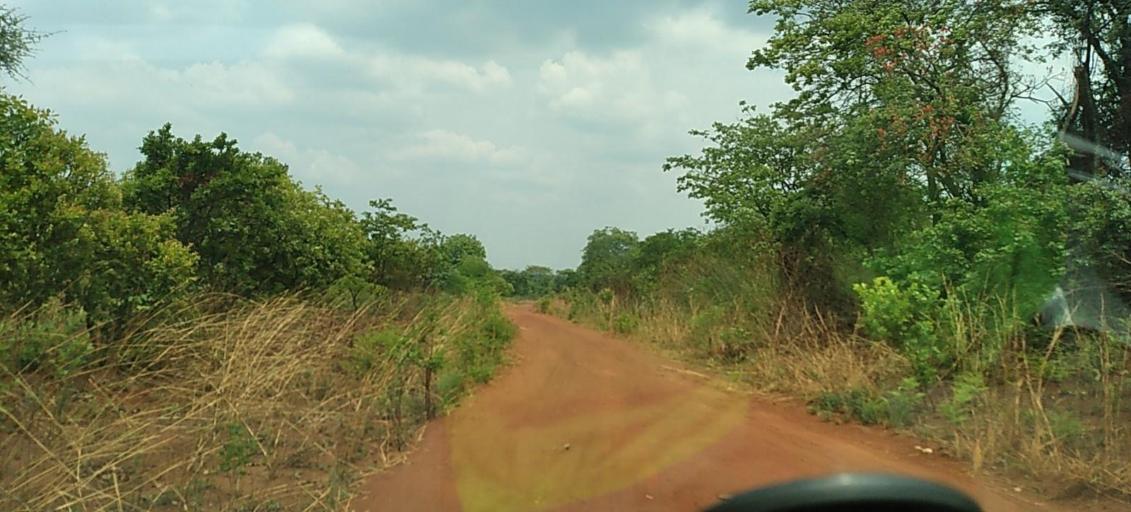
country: ZM
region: North-Western
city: Kansanshi
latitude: -12.0450
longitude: 26.3845
